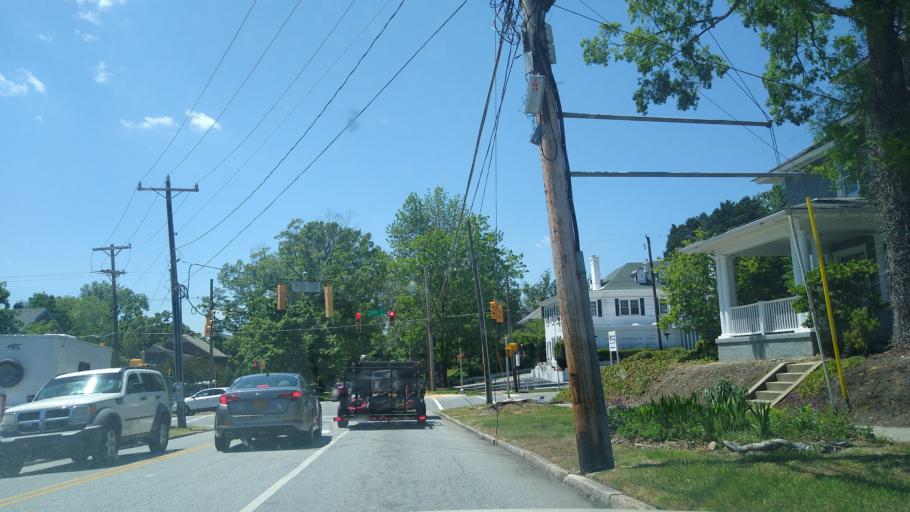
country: US
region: North Carolina
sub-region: Guilford County
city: Greensboro
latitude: 36.0861
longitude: -79.7887
